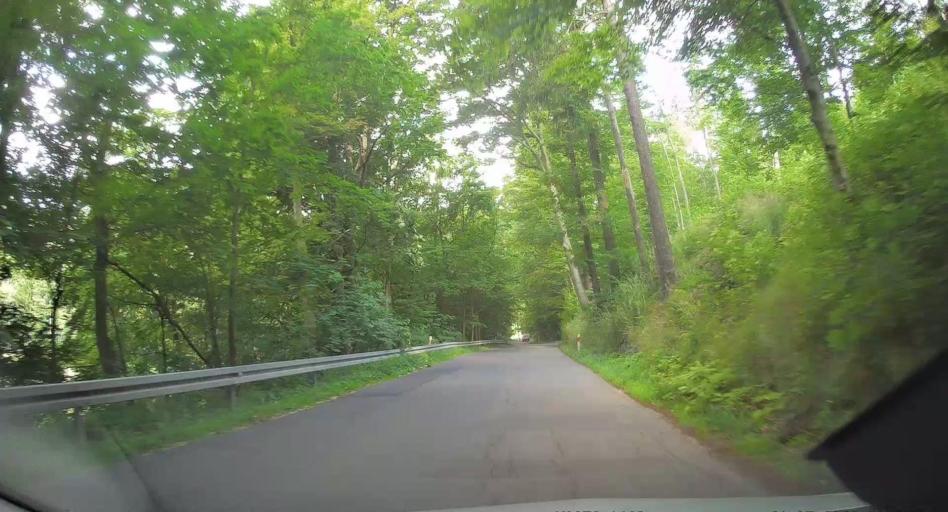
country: PL
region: Lower Silesian Voivodeship
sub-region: Powiat walbrzyski
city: Walim
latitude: 50.7255
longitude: 16.4123
